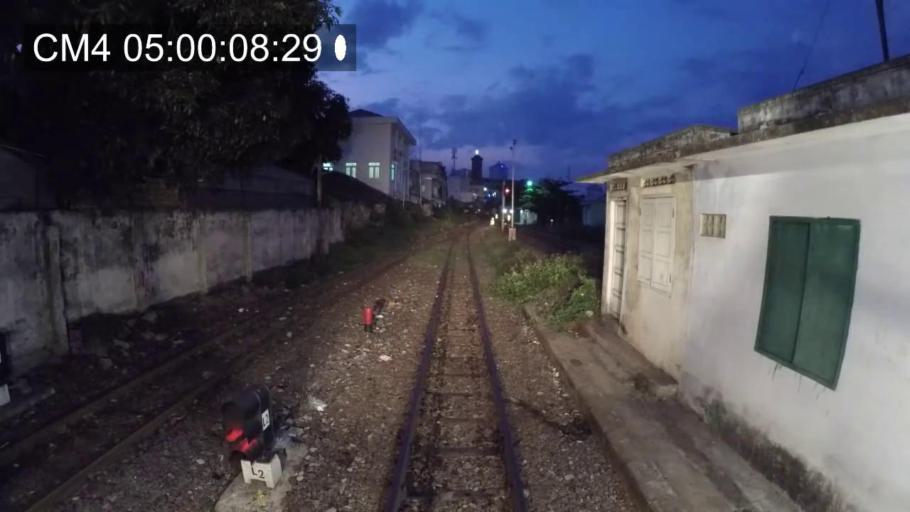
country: VN
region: Khanh Hoa
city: Nha Trang
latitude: 12.2476
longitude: 109.1861
